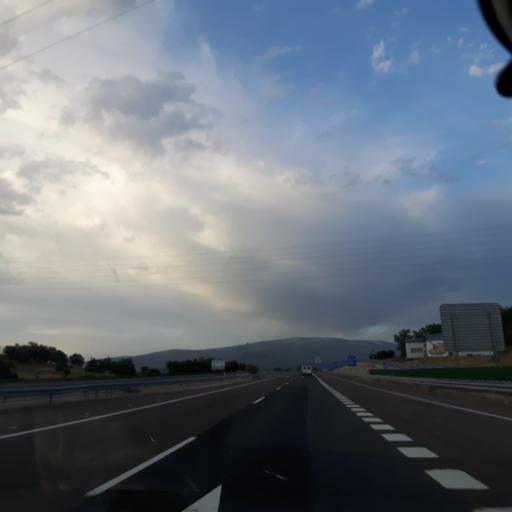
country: ES
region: Castille and Leon
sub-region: Provincia de Salamanca
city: Nava de Bejar
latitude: 40.4874
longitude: -5.6768
